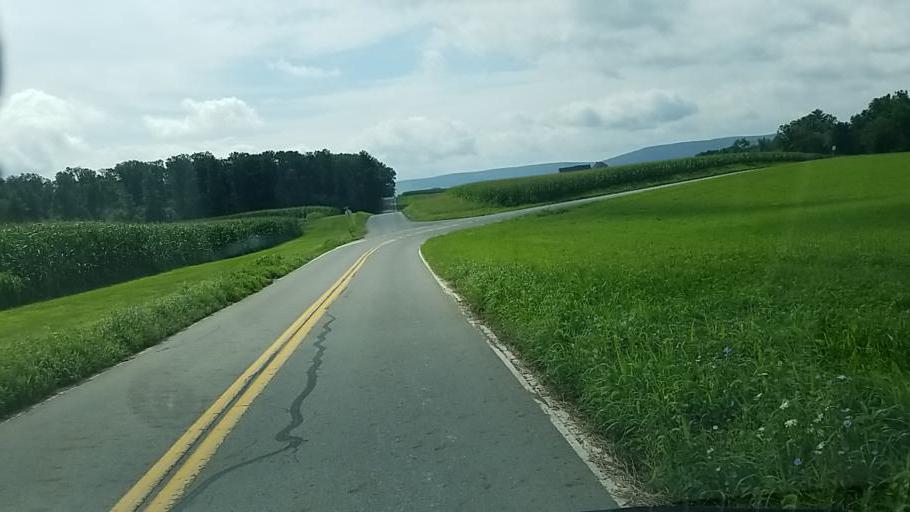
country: US
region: Pennsylvania
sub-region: Dauphin County
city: Elizabethville
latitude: 40.5950
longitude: -76.8824
